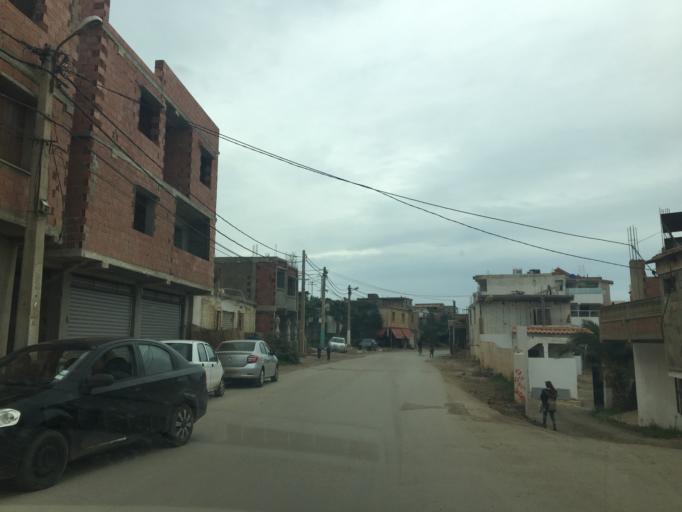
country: DZ
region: Tipaza
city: Tipasa
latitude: 36.6415
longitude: 2.3520
